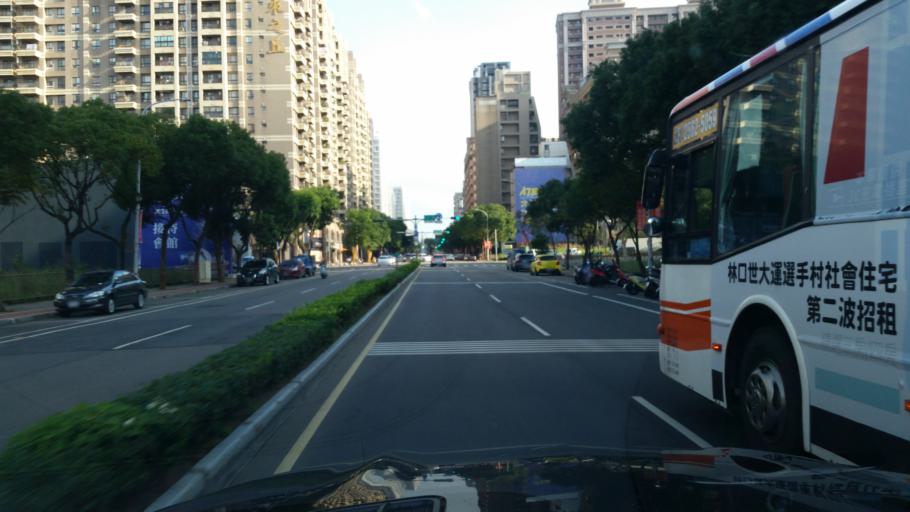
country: TW
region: Taiwan
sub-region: Taoyuan
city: Taoyuan
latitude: 25.0788
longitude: 121.3719
